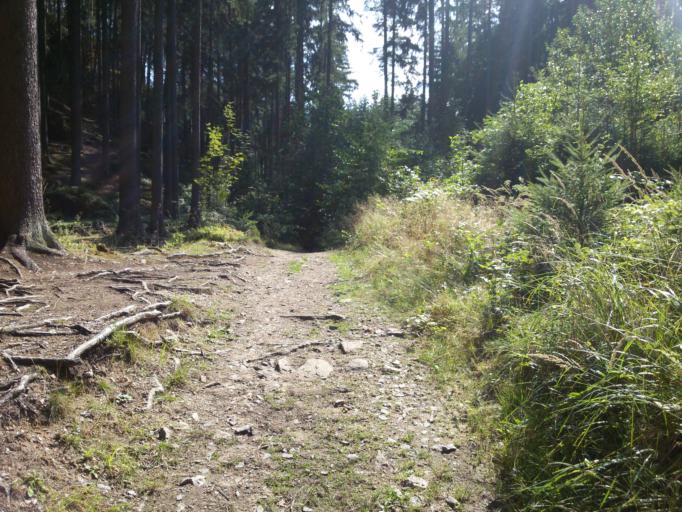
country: CZ
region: Pardubicky
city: Prosec
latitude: 49.8199
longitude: 16.1323
